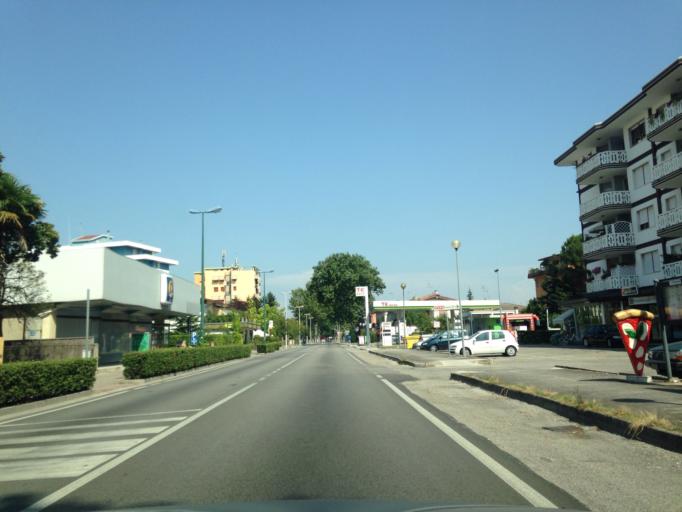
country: IT
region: Veneto
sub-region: Provincia di Venezia
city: Portogruaro
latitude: 45.7750
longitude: 12.8473
